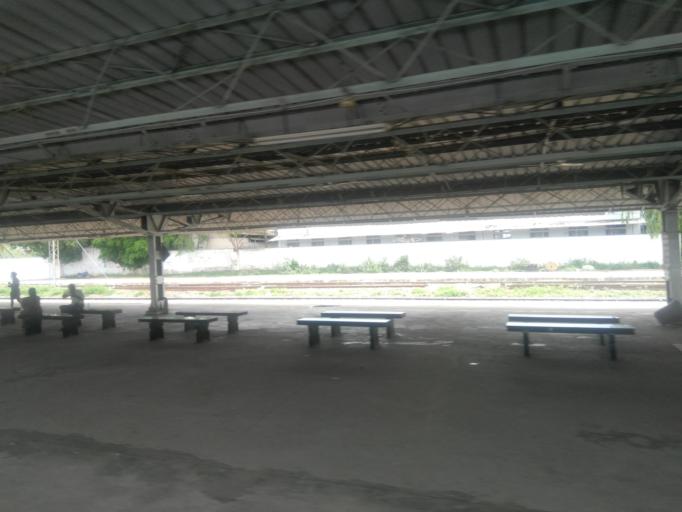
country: IN
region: Tamil Nadu
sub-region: Coimbatore
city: Coimbatore
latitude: 11.0206
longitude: 76.9546
